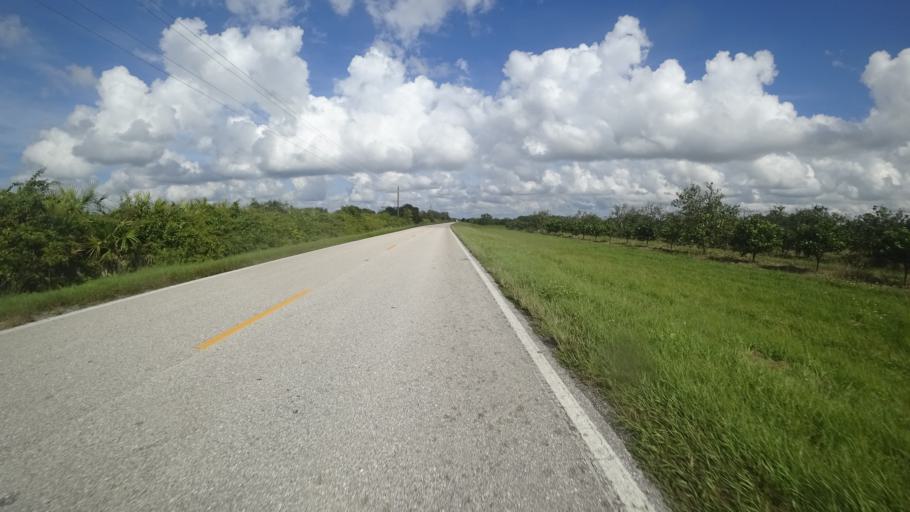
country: US
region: Florida
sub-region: Hillsborough County
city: Wimauma
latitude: 27.5732
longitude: -82.1045
